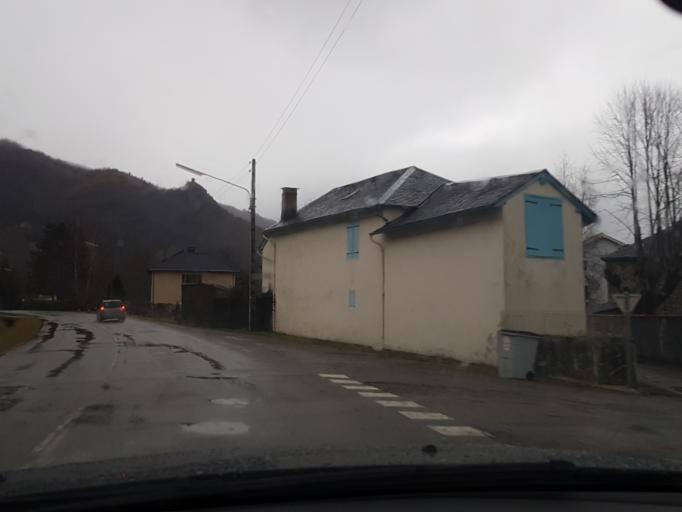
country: FR
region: Midi-Pyrenees
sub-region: Departement de l'Ariege
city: Tarascon-sur-Ariege
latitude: 42.8786
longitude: 1.5413
